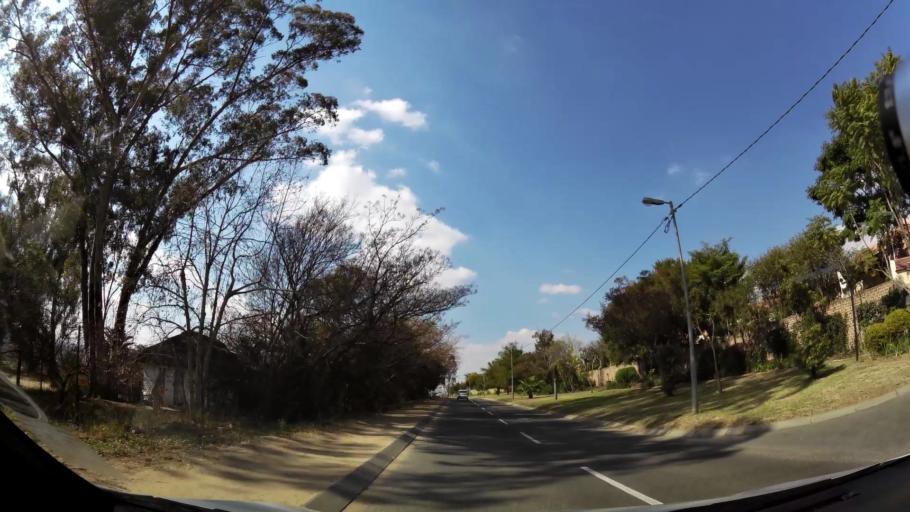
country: ZA
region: Gauteng
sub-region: City of Johannesburg Metropolitan Municipality
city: Midrand
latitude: -26.0083
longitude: 28.0763
